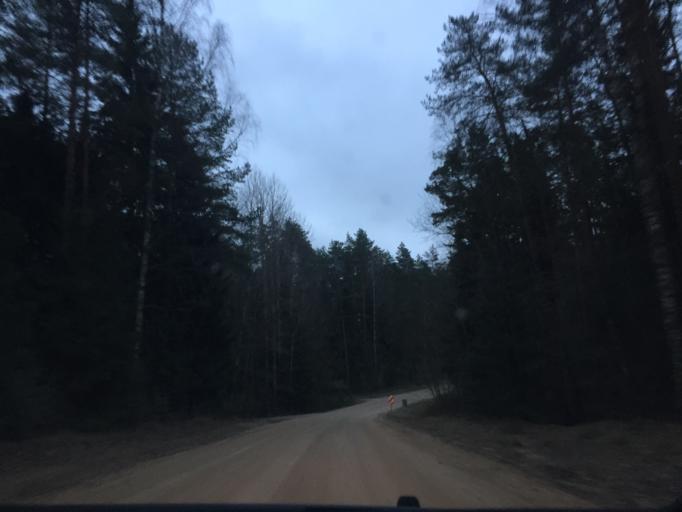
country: LV
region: Cesu Rajons
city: Cesis
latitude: 57.3394
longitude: 25.2630
